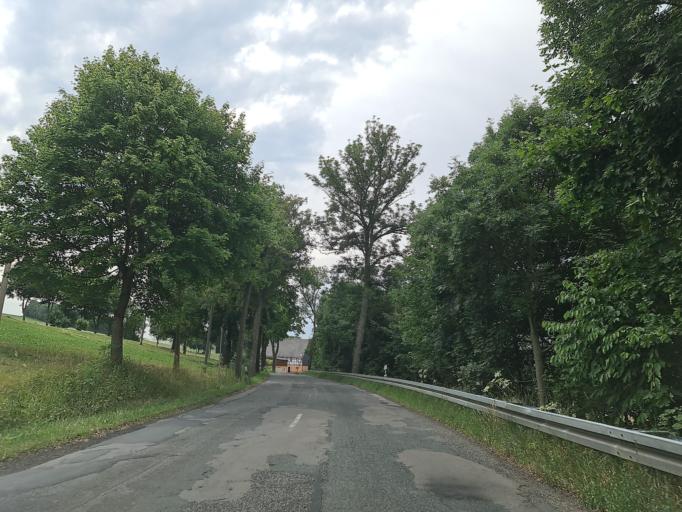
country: DE
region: Saxony
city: Heidersdorf
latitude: 50.7031
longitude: 13.3950
